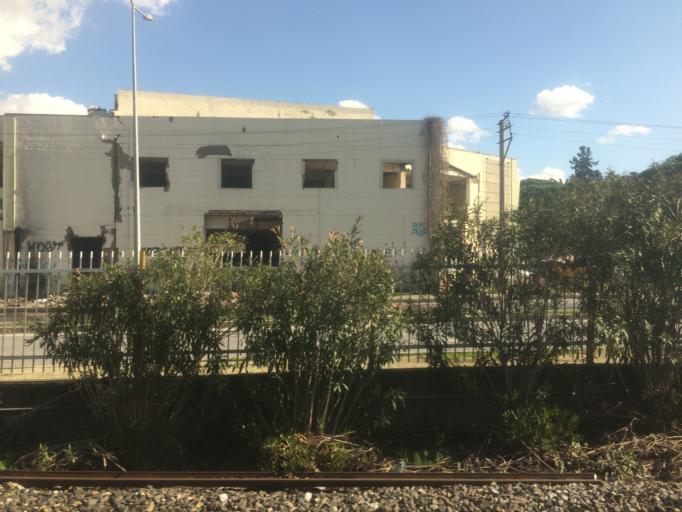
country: TR
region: Izmir
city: Buca
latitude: 38.4407
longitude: 27.1736
